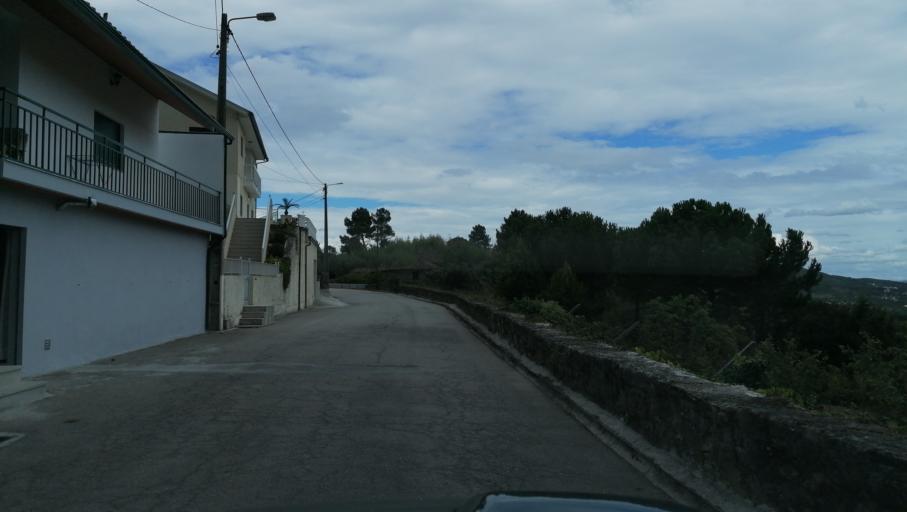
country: PT
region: Vila Real
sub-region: Vila Pouca de Aguiar
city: Vila Pouca de Aguiar
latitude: 41.5497
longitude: -7.6203
